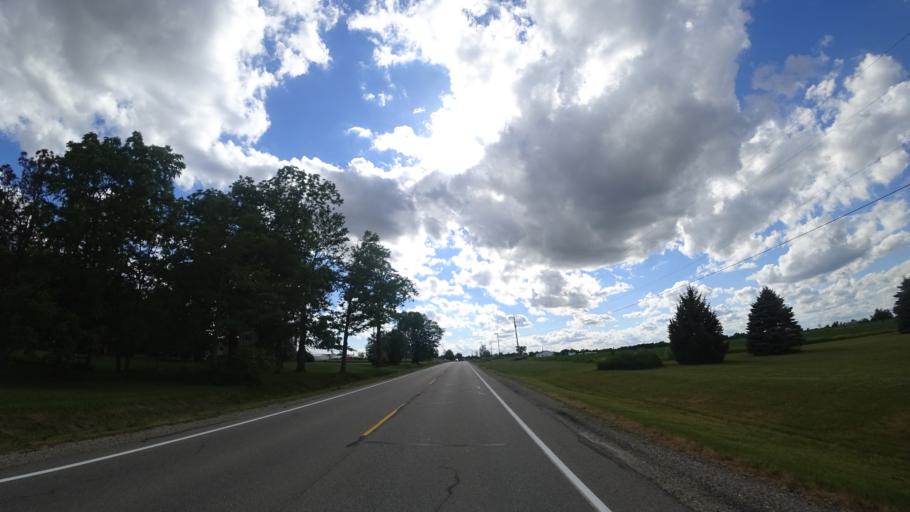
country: US
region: Michigan
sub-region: Ionia County
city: Portland
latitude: 42.8715
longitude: -84.9498
